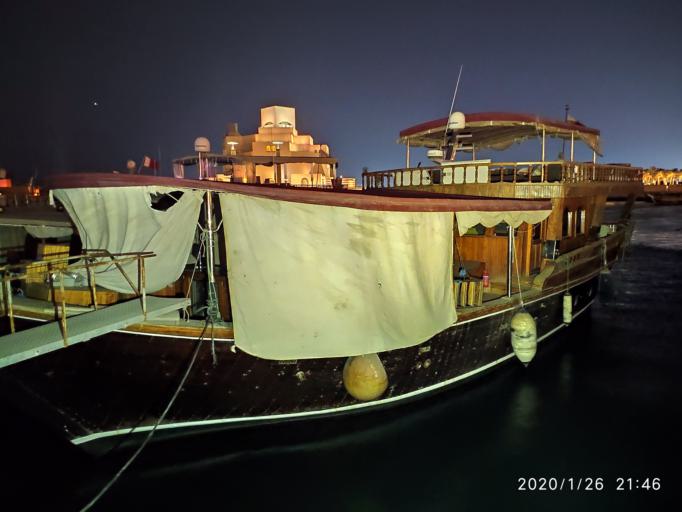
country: QA
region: Baladiyat ad Dawhah
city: Doha
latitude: 25.2938
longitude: 51.5361
